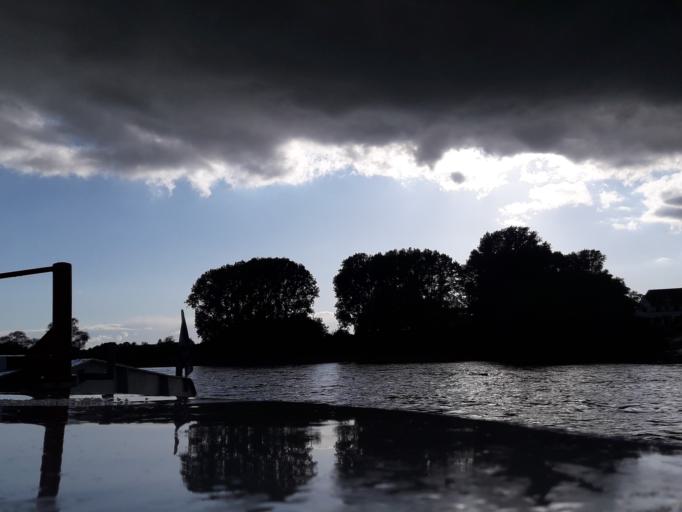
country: DE
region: North Rhine-Westphalia
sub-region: Regierungsbezirk Dusseldorf
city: Meerbusch
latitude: 51.2981
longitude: 6.7265
